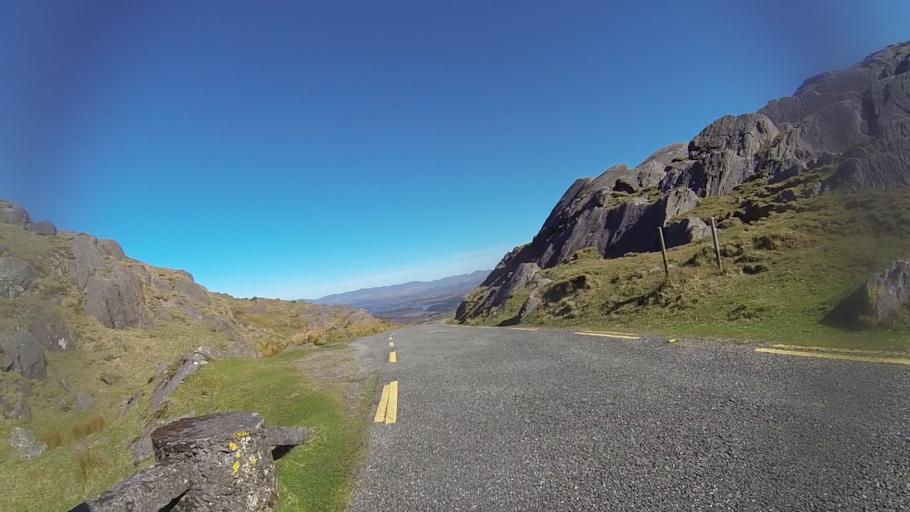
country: IE
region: Munster
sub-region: Ciarrai
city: Kenmare
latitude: 51.7217
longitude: -9.7568
